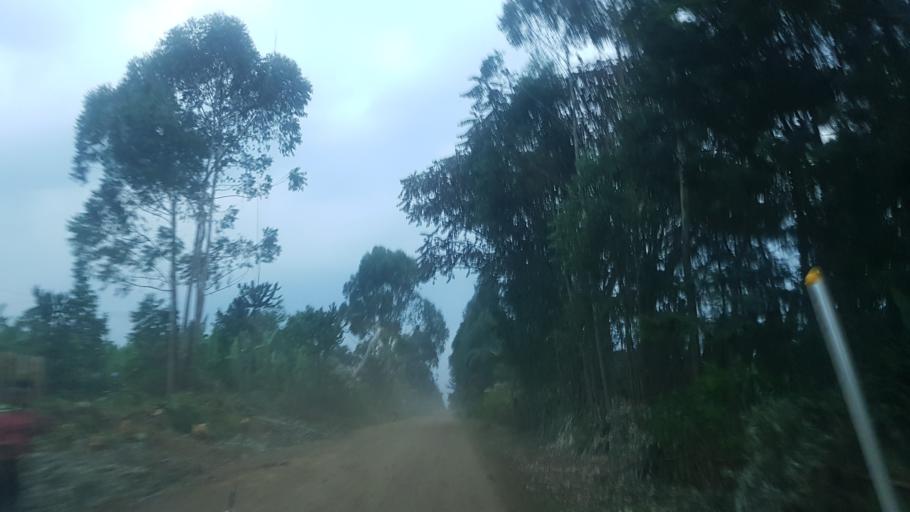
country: ET
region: Oromiya
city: Gore
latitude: 7.7667
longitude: 35.4714
